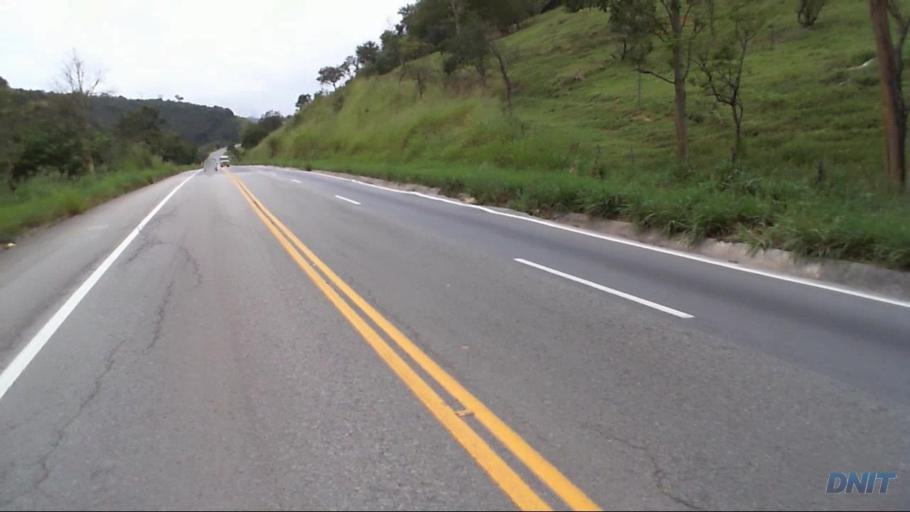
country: BR
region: Minas Gerais
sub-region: Nova Era
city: Nova Era
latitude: -19.7090
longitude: -43.0002
